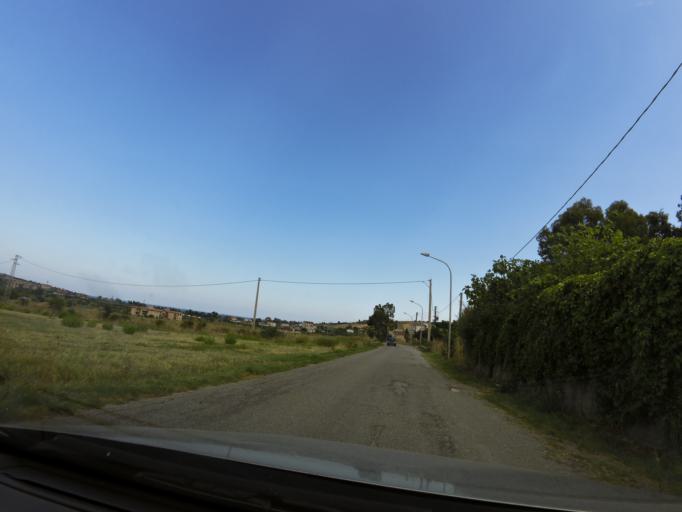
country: IT
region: Calabria
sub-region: Provincia di Reggio Calabria
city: Monasterace
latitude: 38.4243
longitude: 16.5387
